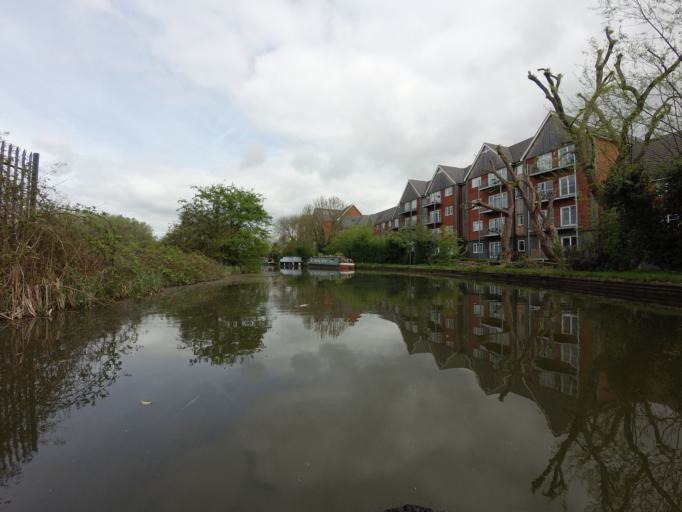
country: GB
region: England
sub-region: Milton Keynes
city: Water Eaton
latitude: 51.9993
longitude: -0.7139
